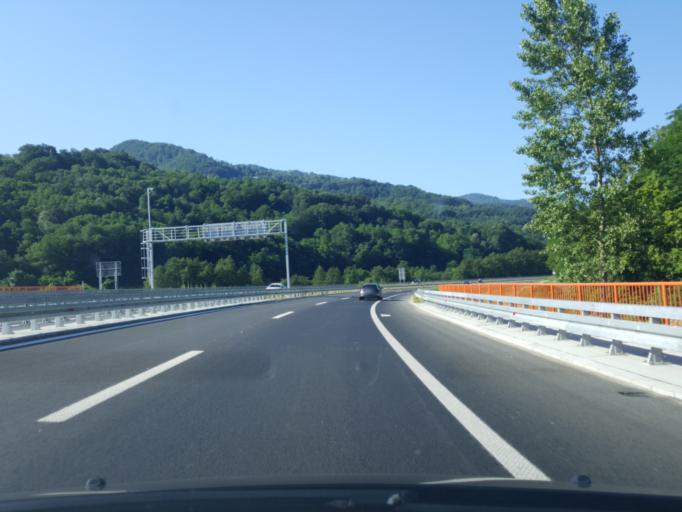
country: RS
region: Central Serbia
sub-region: Pcinjski Okrug
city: Vladicin Han
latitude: 42.8279
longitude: 22.1292
